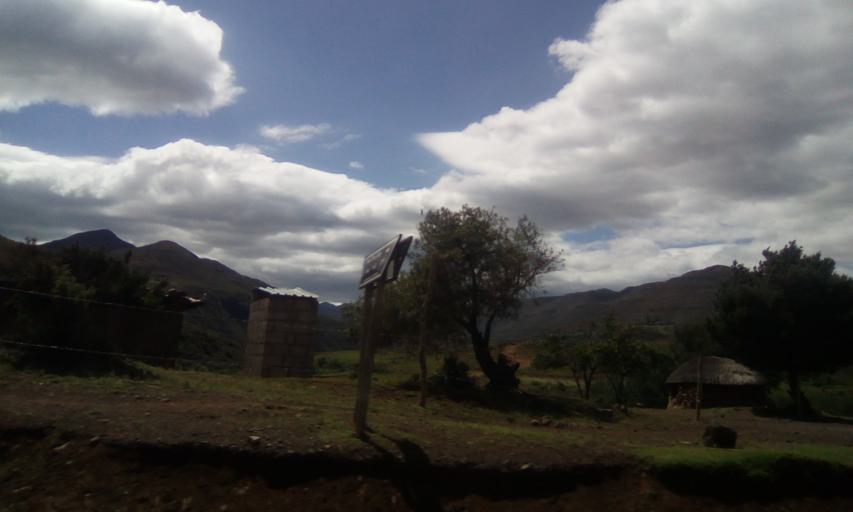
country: LS
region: Maseru
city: Nako
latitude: -29.6626
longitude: 27.8058
